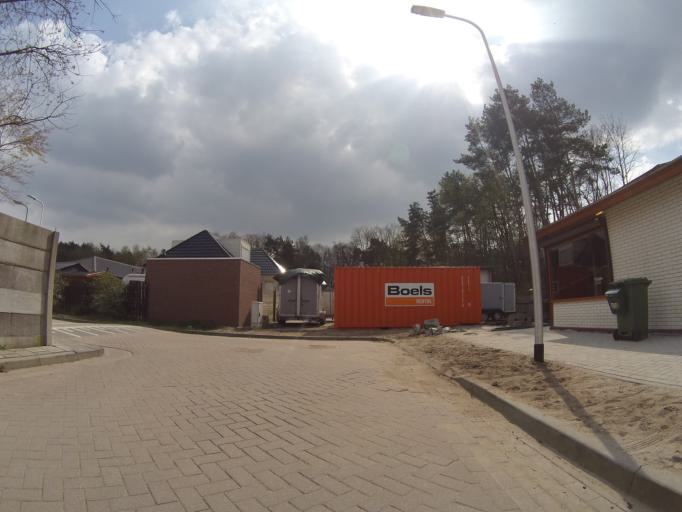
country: NL
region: Utrecht
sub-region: Gemeente Zeist
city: Zeist
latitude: 52.1190
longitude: 5.2698
